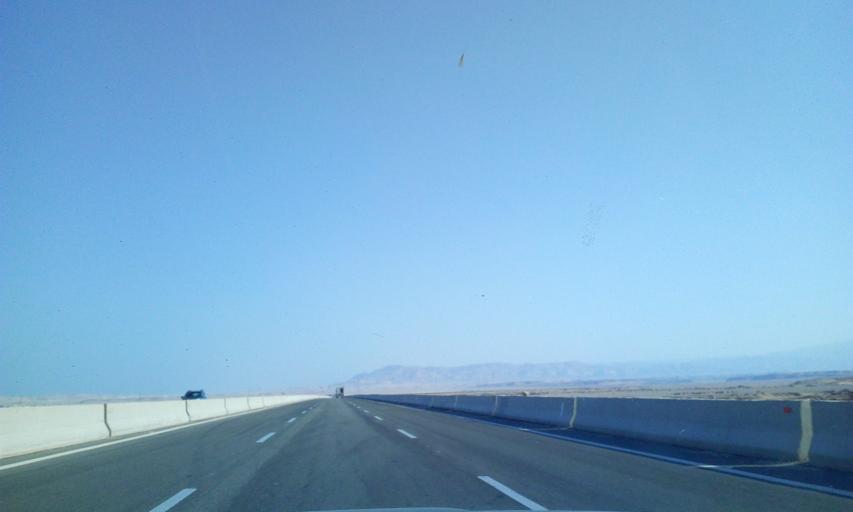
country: EG
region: As Suways
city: Ain Sukhna
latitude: 29.1388
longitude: 32.5205
